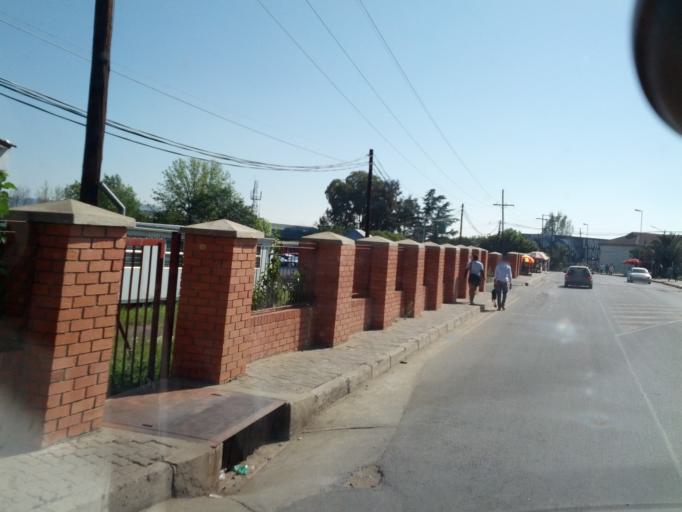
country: LS
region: Maseru
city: Maseru
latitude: -29.3068
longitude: 27.4857
